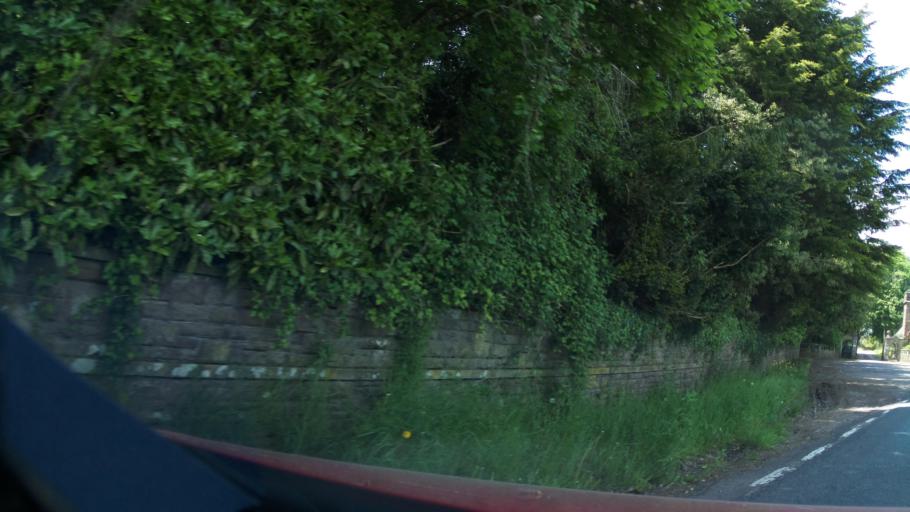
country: GB
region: Wales
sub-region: Monmouthshire
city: Monmouth
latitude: 51.8256
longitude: -2.7471
